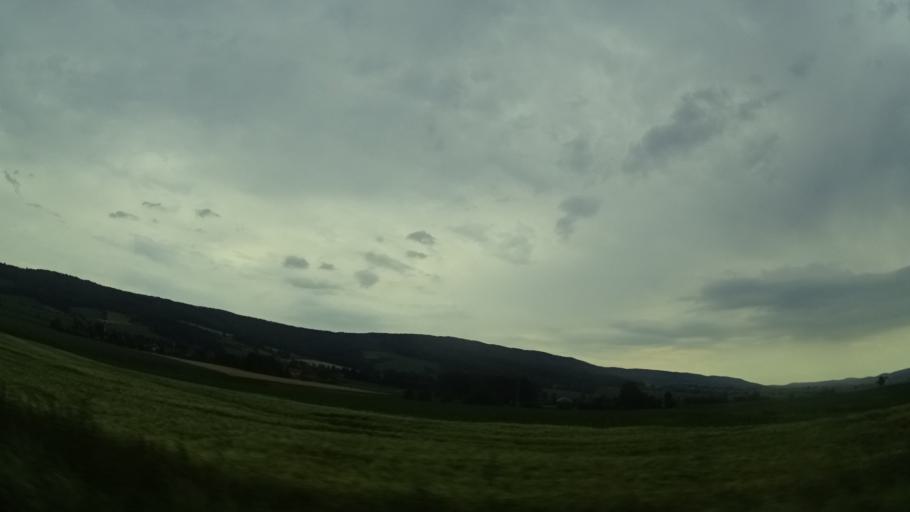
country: DE
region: Lower Saxony
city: Halle
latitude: 52.0057
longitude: 9.5567
